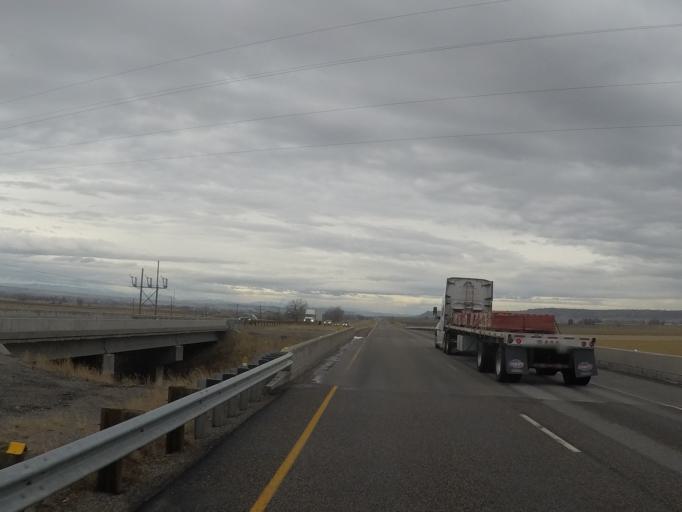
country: US
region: Montana
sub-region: Yellowstone County
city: Laurel
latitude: 45.6571
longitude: -108.8221
